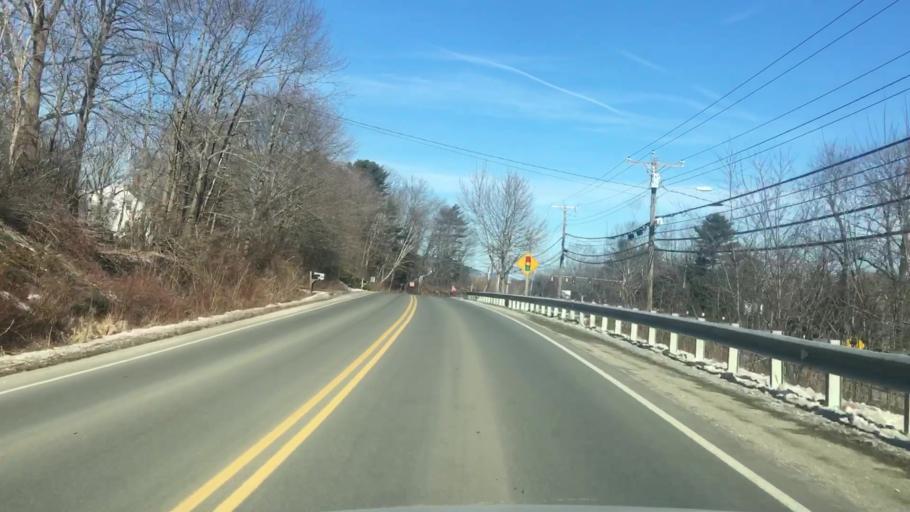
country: US
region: Maine
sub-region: Knox County
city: Rockland
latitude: 44.1415
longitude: -69.0899
